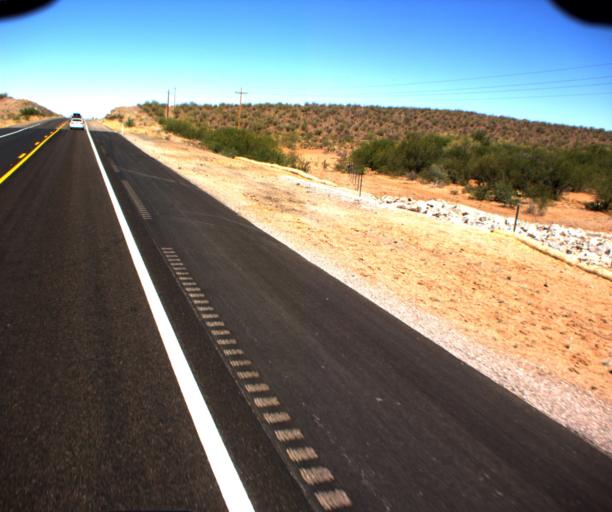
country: US
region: Arizona
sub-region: Pima County
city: Sells
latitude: 31.9167
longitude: -111.8507
